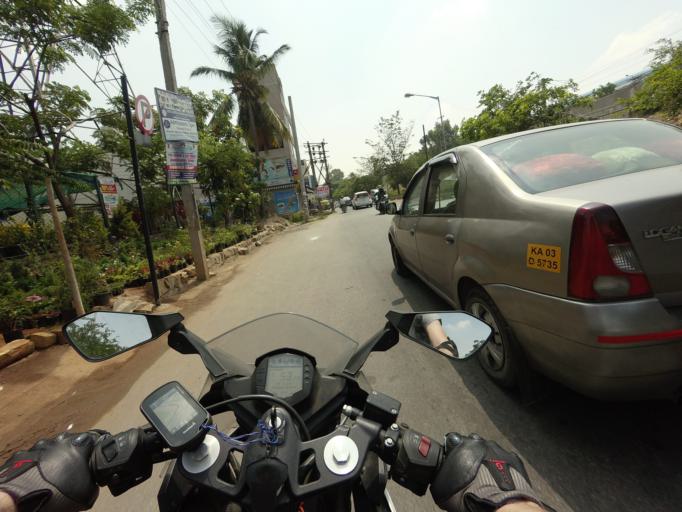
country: IN
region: Karnataka
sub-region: Bangalore Urban
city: Bangalore
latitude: 12.9935
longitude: 77.6565
